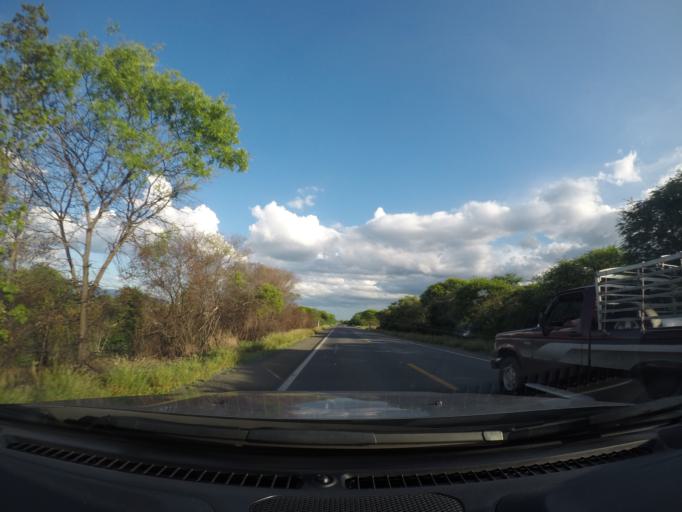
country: BR
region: Bahia
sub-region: Oliveira Dos Brejinhos
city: Beira Rio
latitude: -12.2266
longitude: -42.7854
